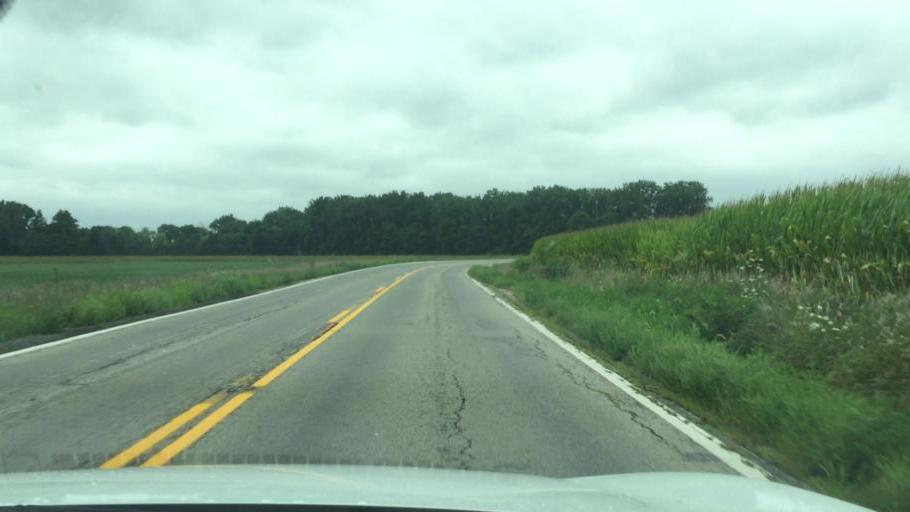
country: US
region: Ohio
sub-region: Champaign County
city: North Lewisburg
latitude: 40.2277
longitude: -83.5170
